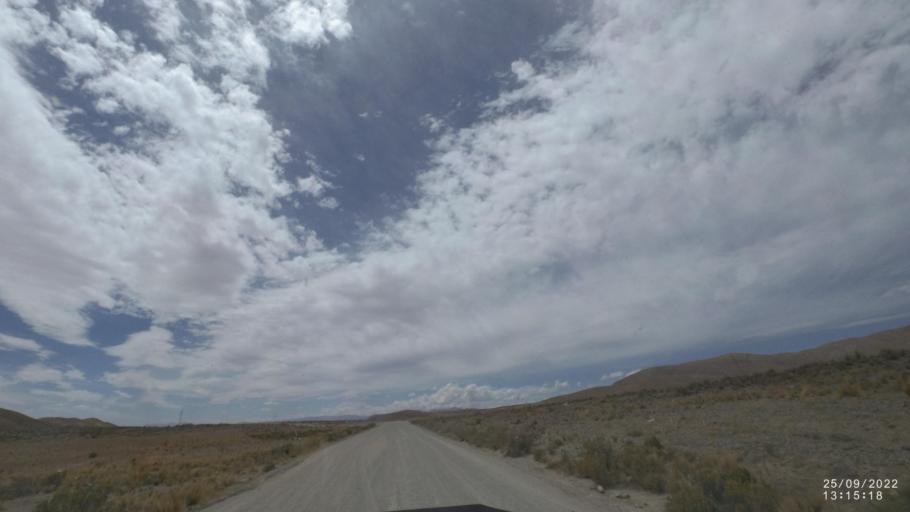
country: BO
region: Oruro
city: Oruro
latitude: -17.9296
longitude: -67.0409
